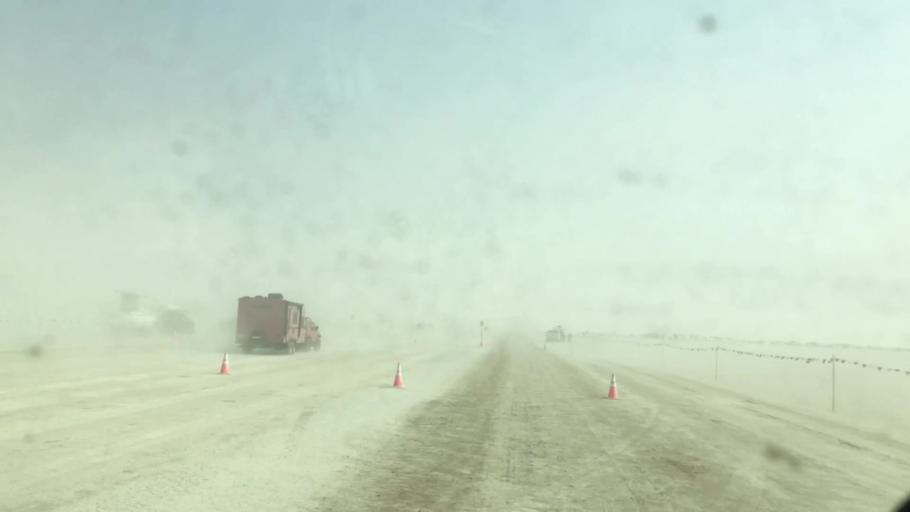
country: US
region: Nevada
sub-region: Pershing County
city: Lovelock
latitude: 40.7627
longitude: -119.2505
